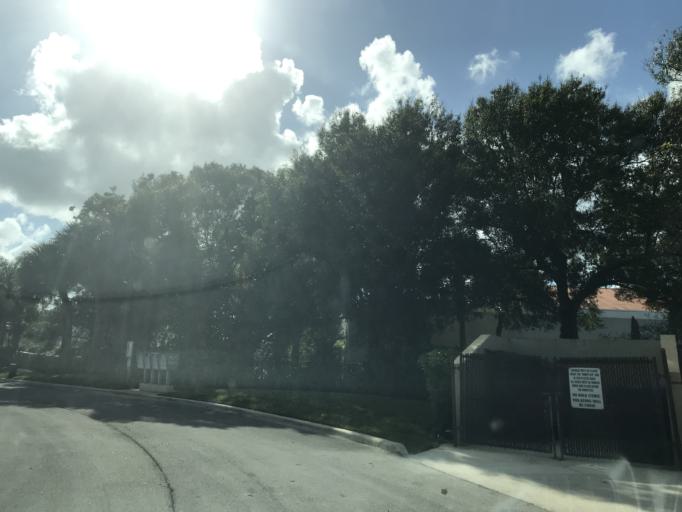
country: US
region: Florida
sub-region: Broward County
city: Coconut Creek
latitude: 26.2575
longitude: -80.1904
